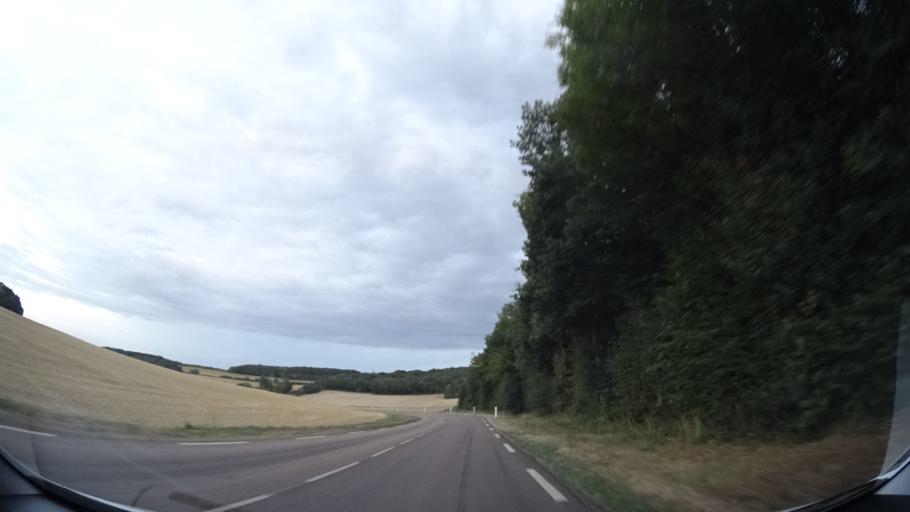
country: FR
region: Bourgogne
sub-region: Departement de l'Yonne
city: Saint-Julien-du-Sault
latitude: 47.9319
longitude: 3.2175
